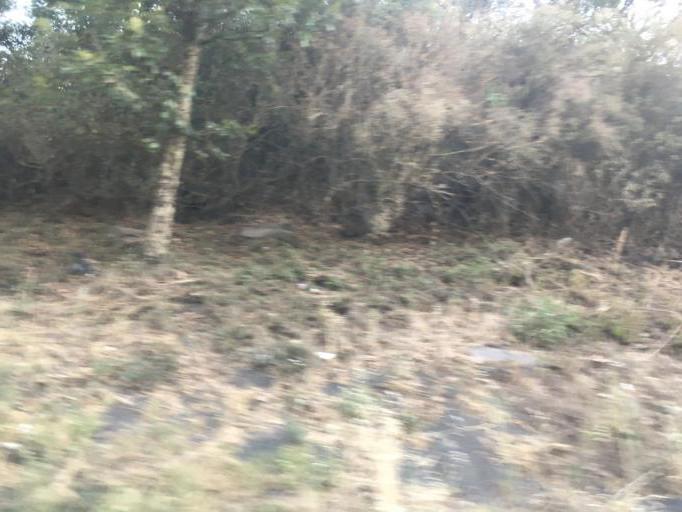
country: MX
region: Michoacan
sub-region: Morelia
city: Iratzio
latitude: 19.6226
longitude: -101.4625
